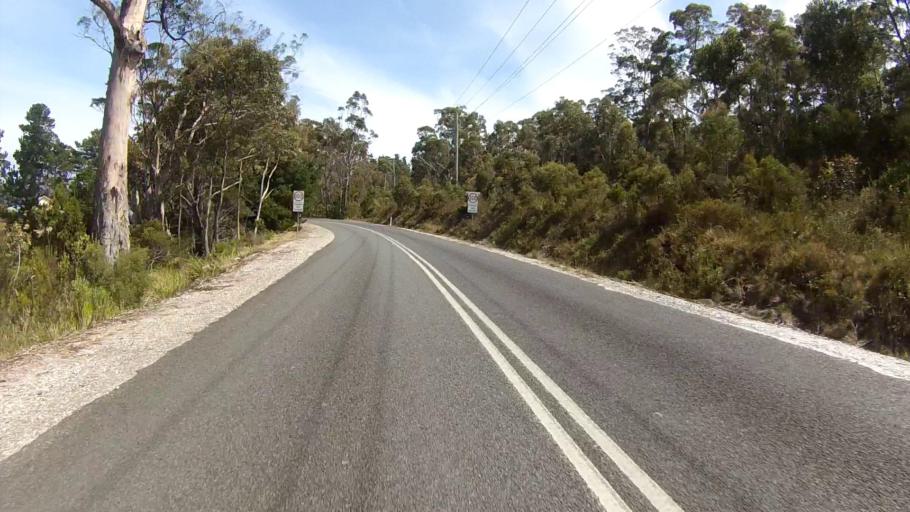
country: AU
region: Tasmania
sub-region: Huon Valley
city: Cygnet
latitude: -43.2681
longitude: 147.1466
